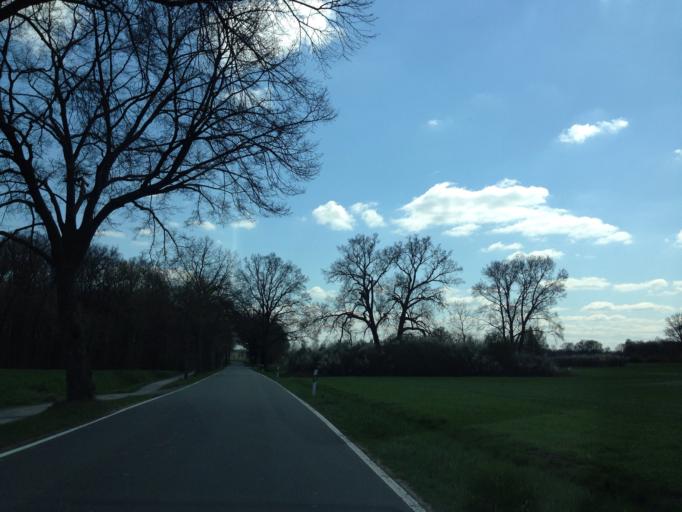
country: DE
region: North Rhine-Westphalia
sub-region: Regierungsbezirk Munster
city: Muenster
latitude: 51.9810
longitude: 7.5770
